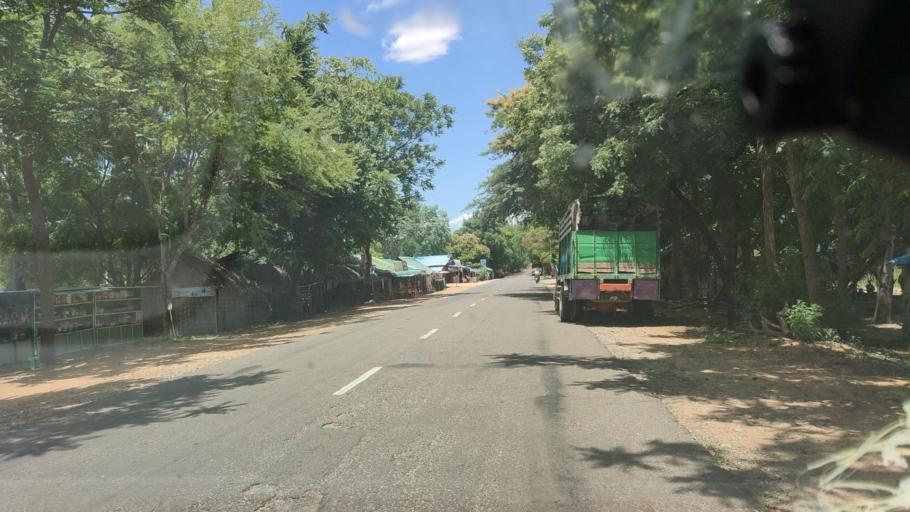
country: MM
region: Magway
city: Chauk
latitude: 20.8424
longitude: 94.8857
